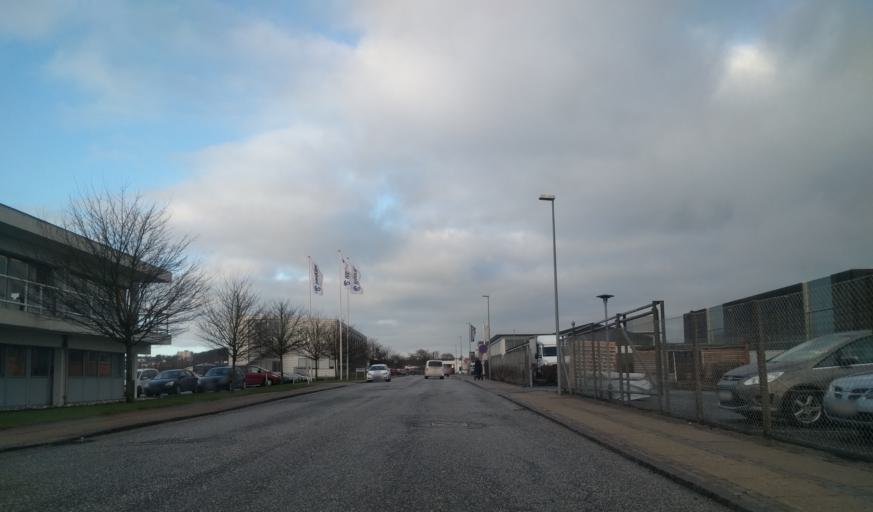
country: DK
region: North Denmark
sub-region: Alborg Kommune
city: Aalborg
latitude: 57.0339
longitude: 9.9265
